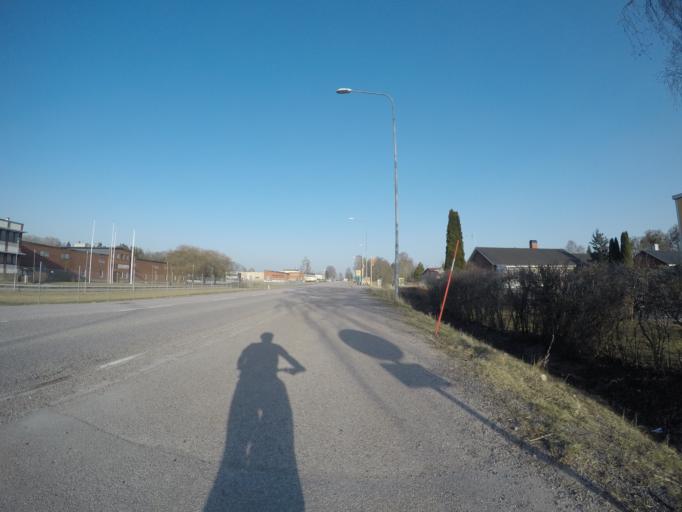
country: SE
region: Vaestmanland
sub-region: Kungsors Kommun
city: Kungsoer
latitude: 59.4256
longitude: 16.1174
